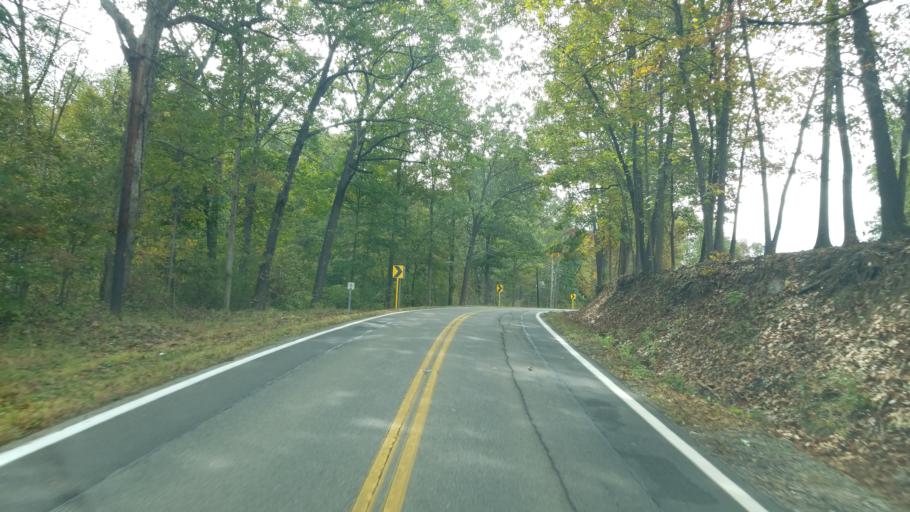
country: US
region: Ohio
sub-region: Jackson County
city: Wellston
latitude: 39.1148
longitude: -82.5627
